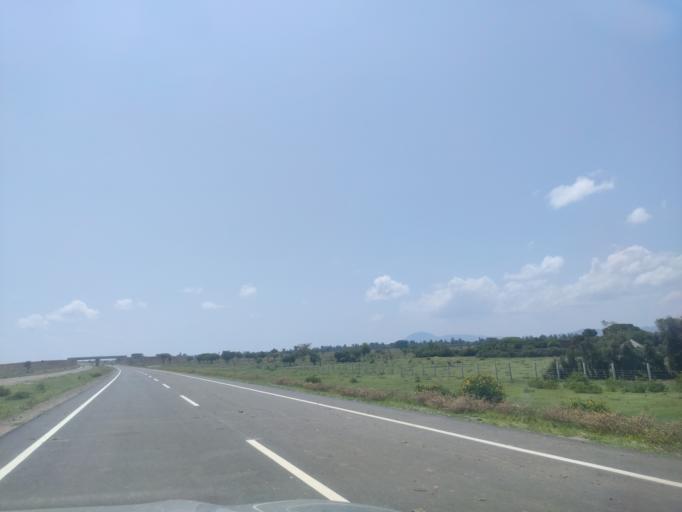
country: ET
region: Oromiya
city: Ziway
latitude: 8.2294
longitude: 38.8719
